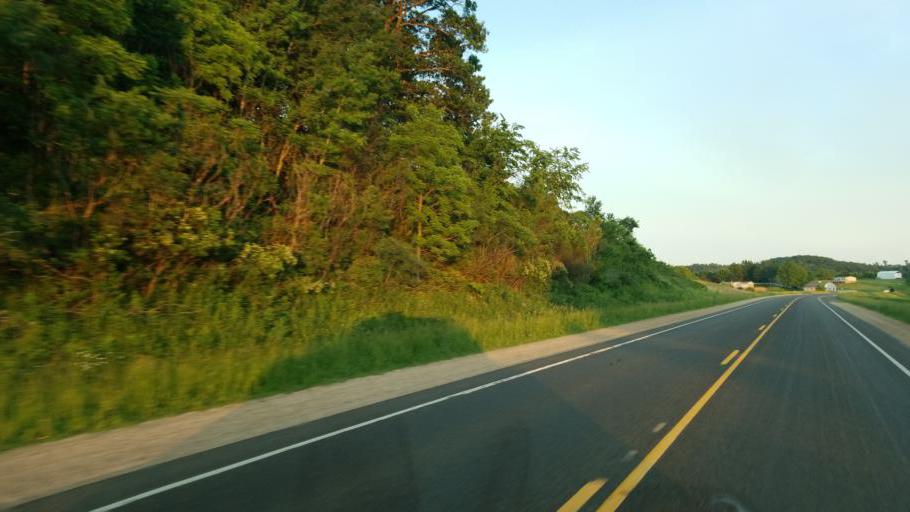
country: US
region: Wisconsin
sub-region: Monroe County
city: Tomah
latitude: 43.9216
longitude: -90.4976
